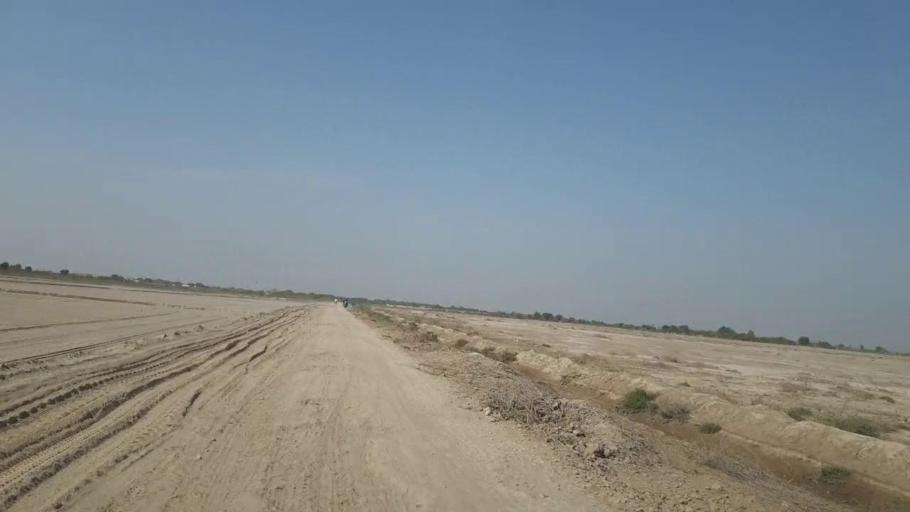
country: PK
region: Sindh
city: Nabisar
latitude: 25.0128
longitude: 69.5269
